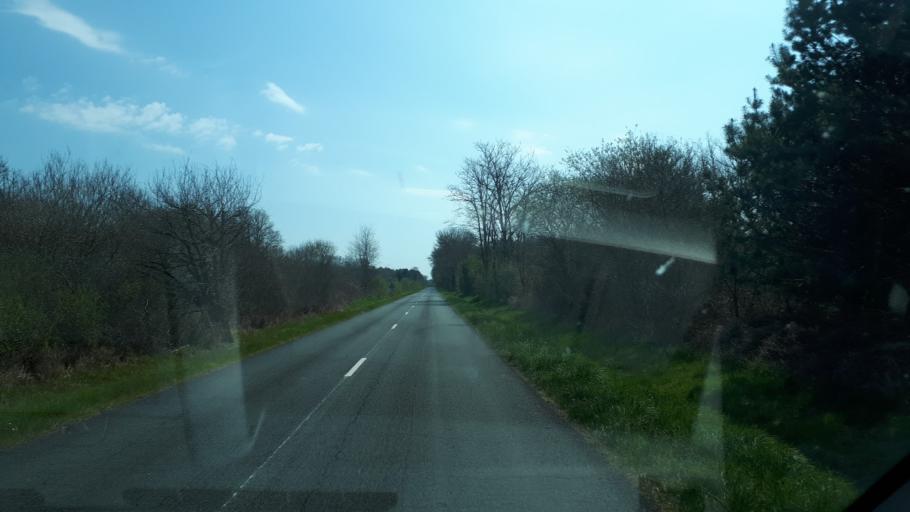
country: FR
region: Centre
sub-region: Departement du Loir-et-Cher
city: Selles-Saint-Denis
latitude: 47.3472
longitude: 1.8760
